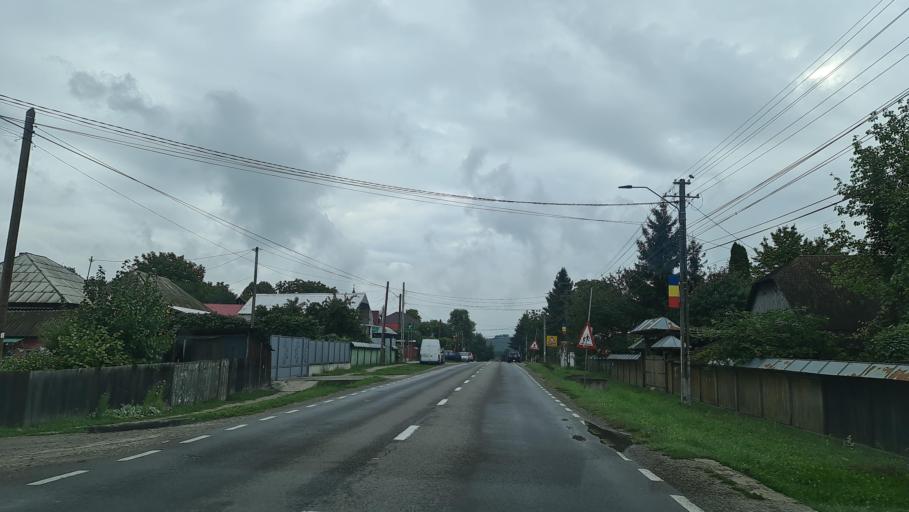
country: RO
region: Neamt
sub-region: Comuna Borlesti
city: Mastacan
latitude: 46.7768
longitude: 26.5028
